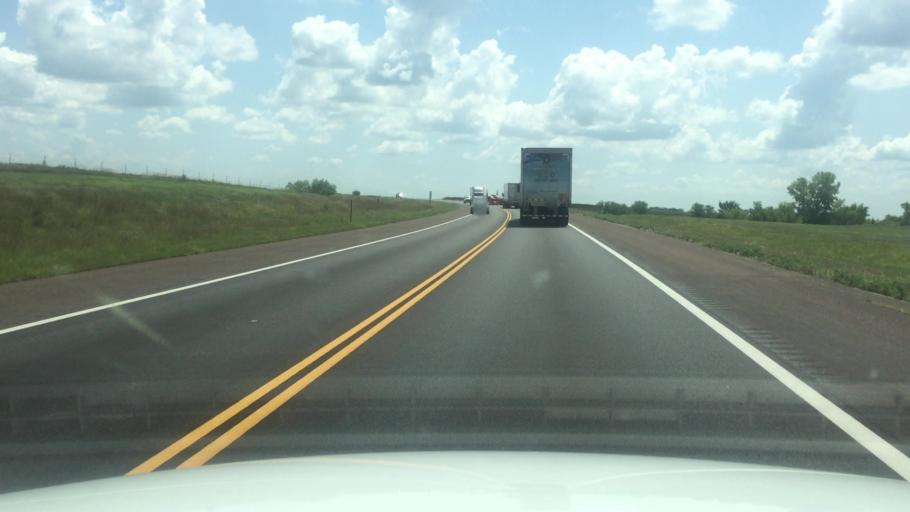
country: US
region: Kansas
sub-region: Nemaha County
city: Sabetha
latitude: 39.8700
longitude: -95.7773
